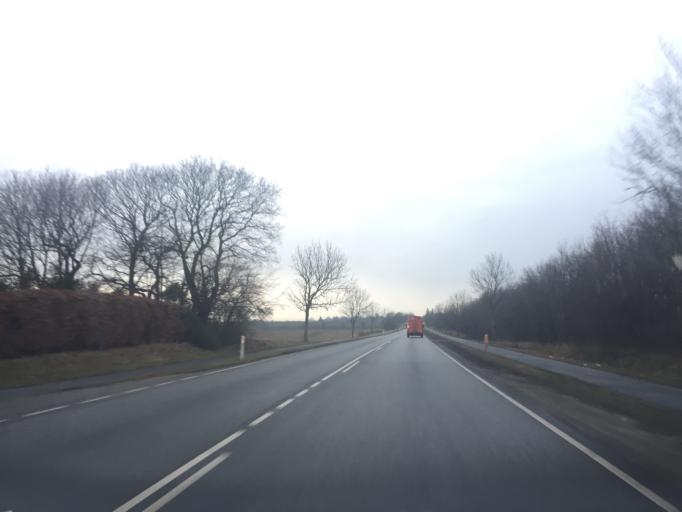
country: DK
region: Zealand
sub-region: Solrod Kommune
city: Solrod Strand
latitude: 55.5769
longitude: 12.2352
